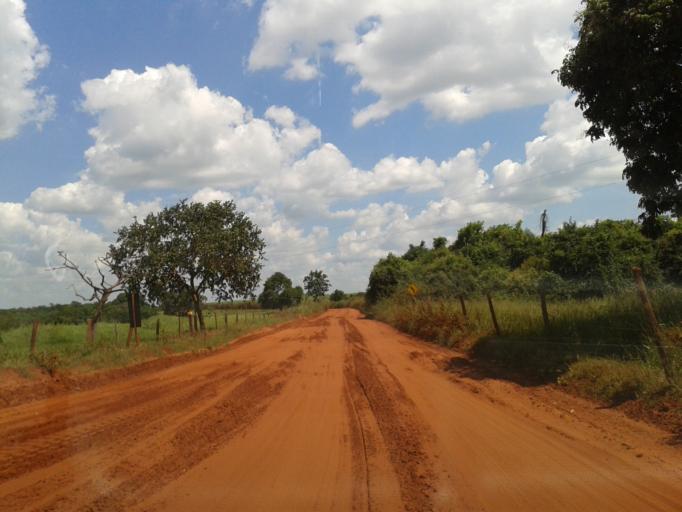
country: BR
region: Minas Gerais
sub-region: Ituiutaba
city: Ituiutaba
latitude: -19.0698
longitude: -49.7268
